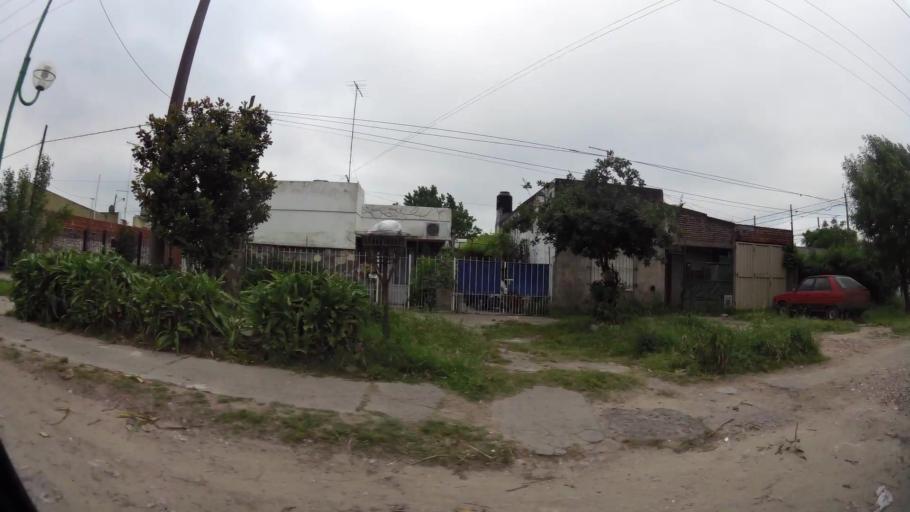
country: AR
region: Buenos Aires
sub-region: Partido de La Plata
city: La Plata
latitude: -34.9325
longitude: -57.9915
